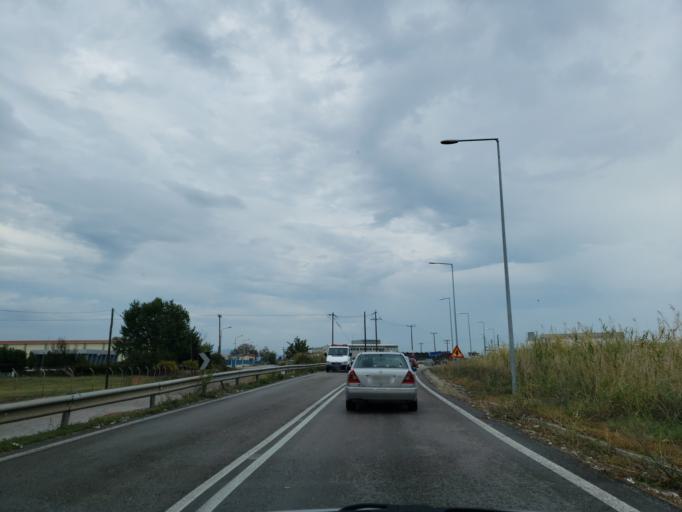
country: GR
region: Central Greece
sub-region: Nomos Voiotias
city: Livadeia
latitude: 38.4681
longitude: 22.9211
